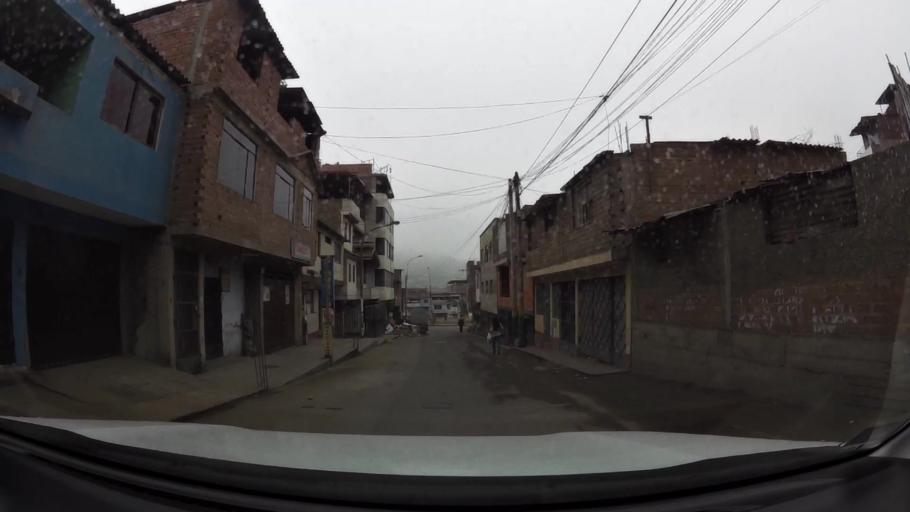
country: PE
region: Lima
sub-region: Lima
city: Surco
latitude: -12.1561
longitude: -76.9500
